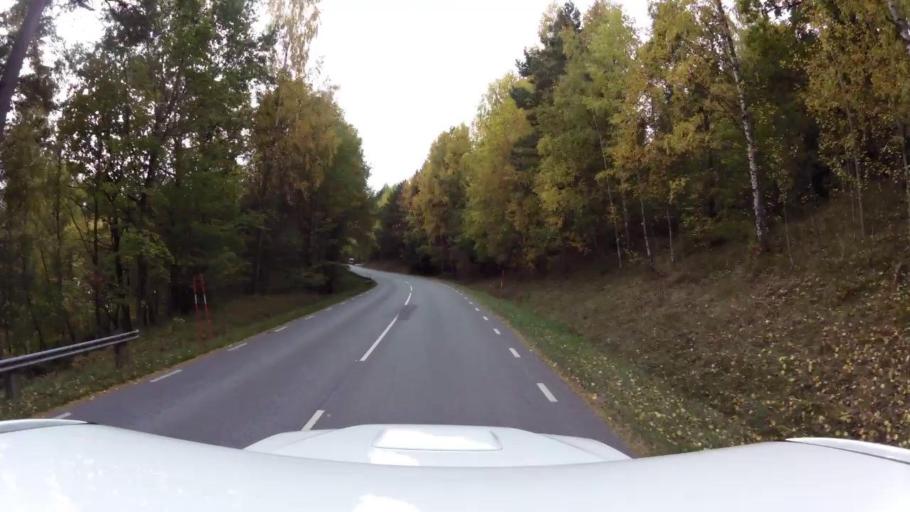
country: SE
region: OEstergoetland
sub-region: Linkopings Kommun
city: Ekangen
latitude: 58.5405
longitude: 15.6180
